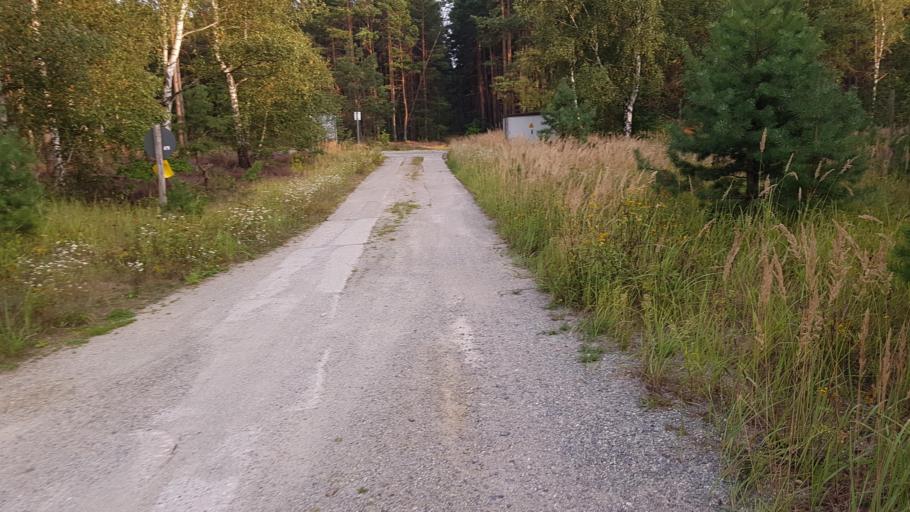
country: DE
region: Brandenburg
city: Schonborn
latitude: 51.6283
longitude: 13.5060
